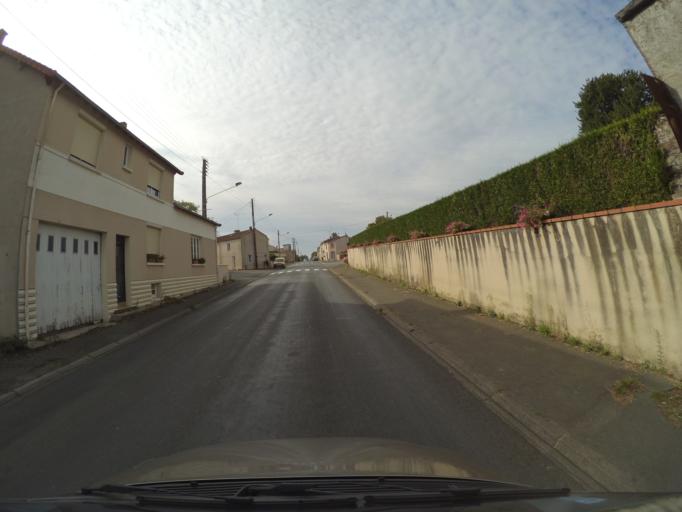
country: FR
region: Pays de la Loire
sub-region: Departement de Maine-et-Loire
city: Villedieu-la-Blouere
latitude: 47.1578
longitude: -1.0536
